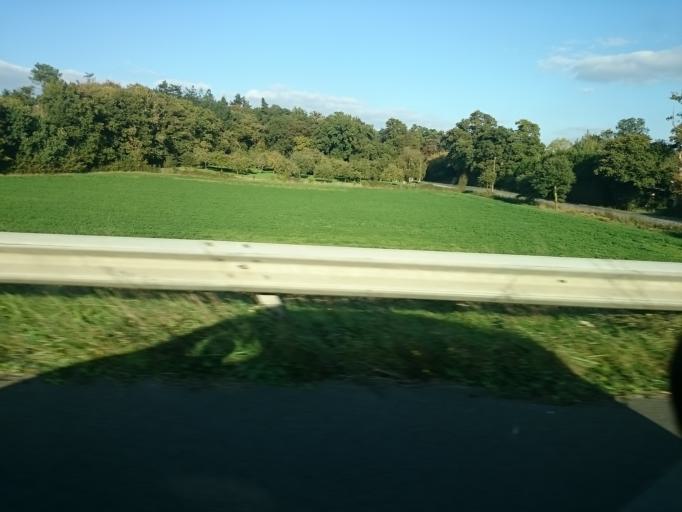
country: FR
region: Pays de la Loire
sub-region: Departement de la Loire-Atlantique
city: Derval
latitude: 47.6645
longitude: -1.6825
